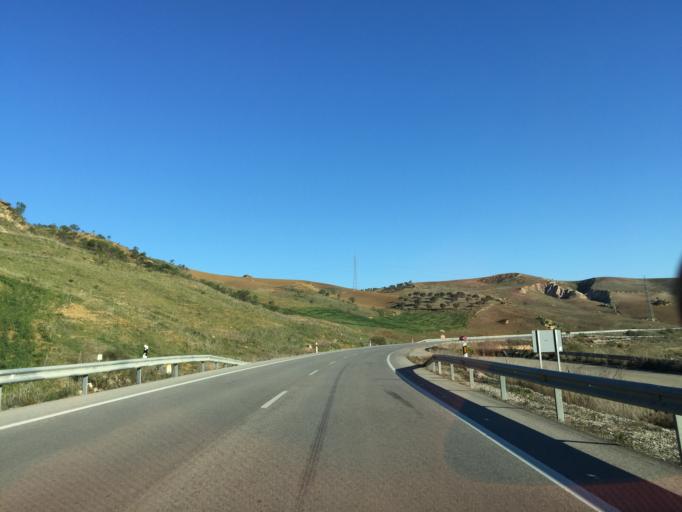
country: ES
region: Andalusia
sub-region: Provincia de Malaga
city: Ardales
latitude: 36.8932
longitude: -4.8486
